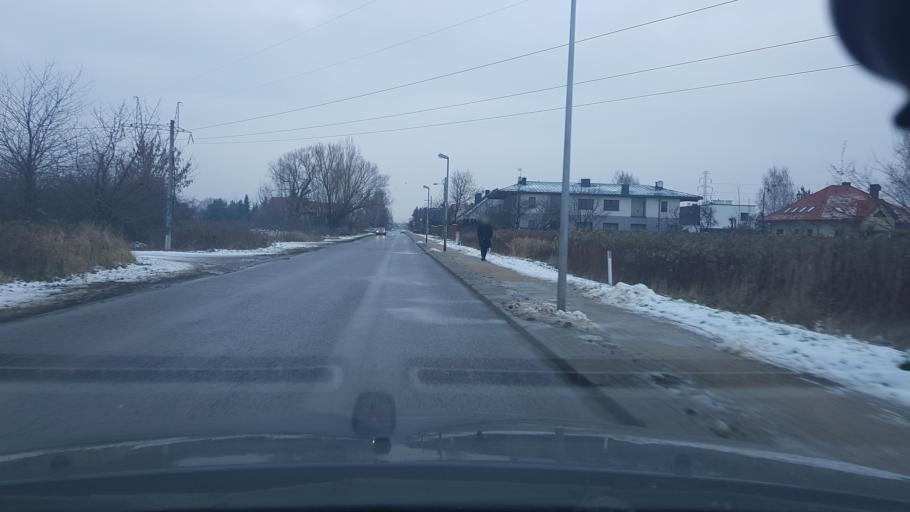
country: PL
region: Masovian Voivodeship
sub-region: Warszawa
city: Targowek
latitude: 52.3105
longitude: 21.0396
